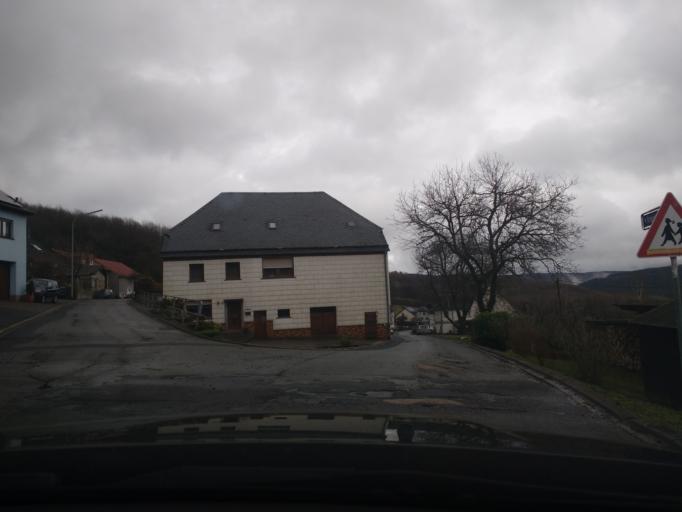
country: DE
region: Rheinland-Pfalz
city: Lampaden
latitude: 49.6484
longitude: 6.7028
